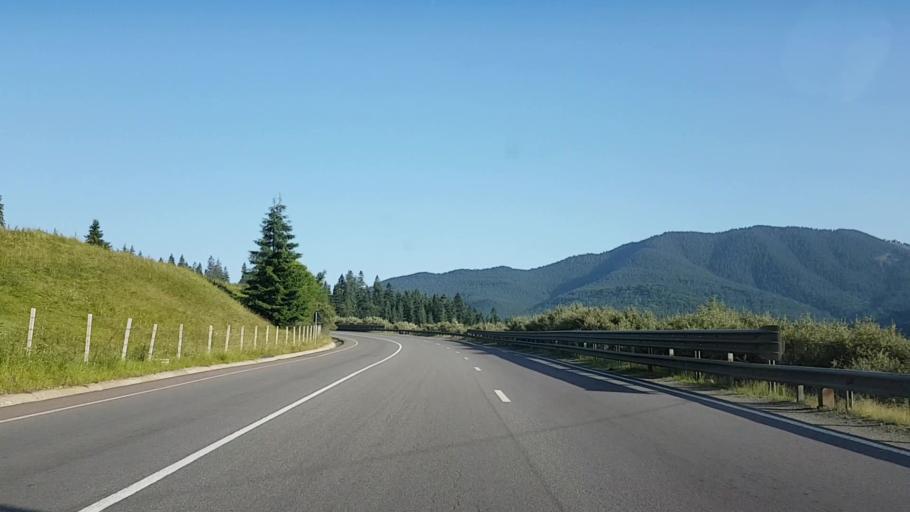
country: RO
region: Bistrita-Nasaud
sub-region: Comuna Lunca Ilvei
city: Lunca Ilvei
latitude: 47.2296
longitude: 24.9668
